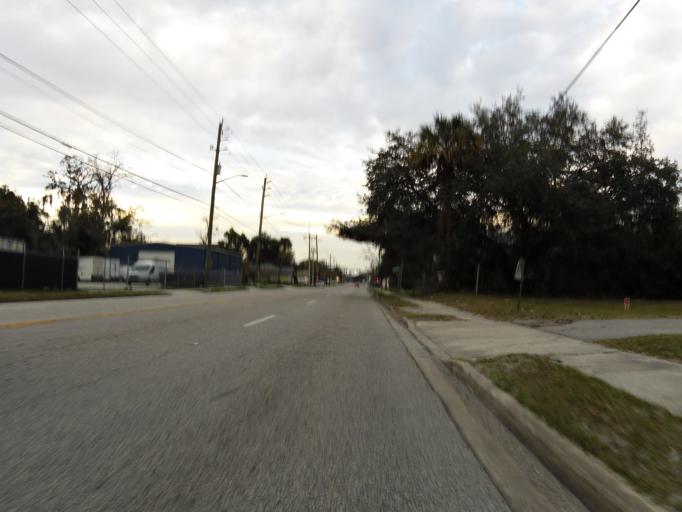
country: US
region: Florida
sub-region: Duval County
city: Jacksonville
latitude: 30.2833
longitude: -81.6437
